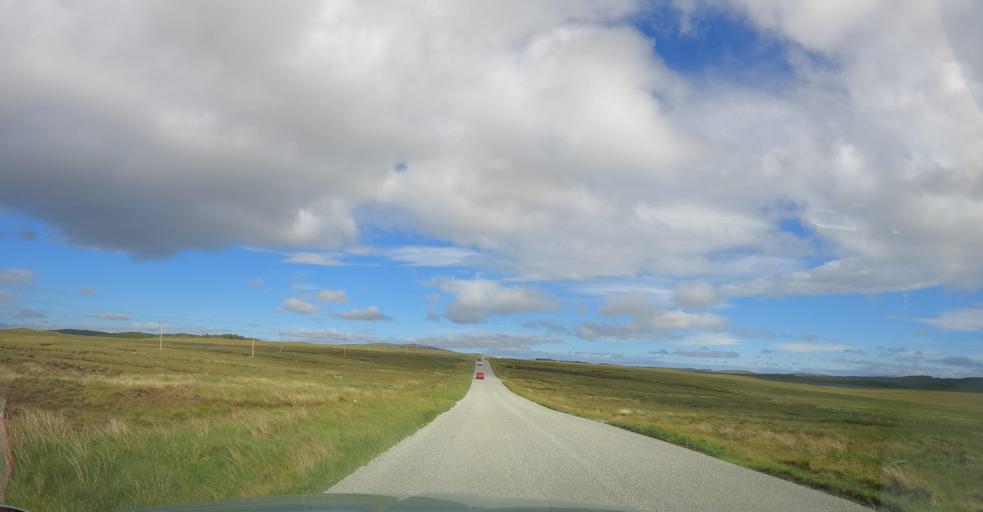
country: GB
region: Scotland
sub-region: Eilean Siar
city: Isle of Lewis
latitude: 58.1867
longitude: -6.6863
